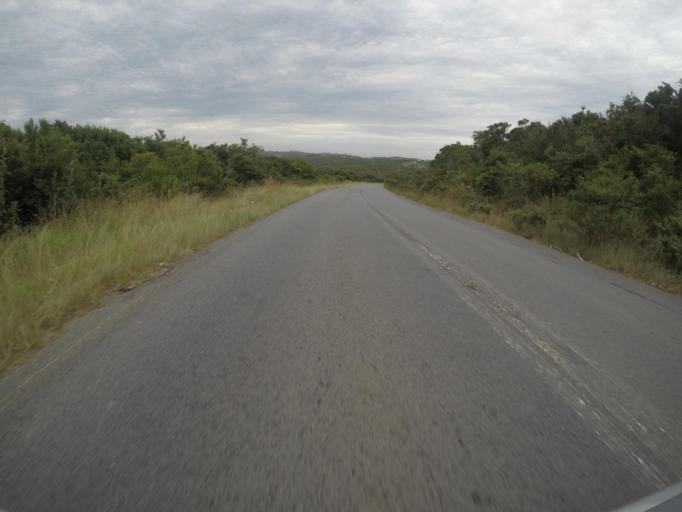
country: ZA
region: Eastern Cape
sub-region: Buffalo City Metropolitan Municipality
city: East London
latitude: -32.9445
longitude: 27.9290
